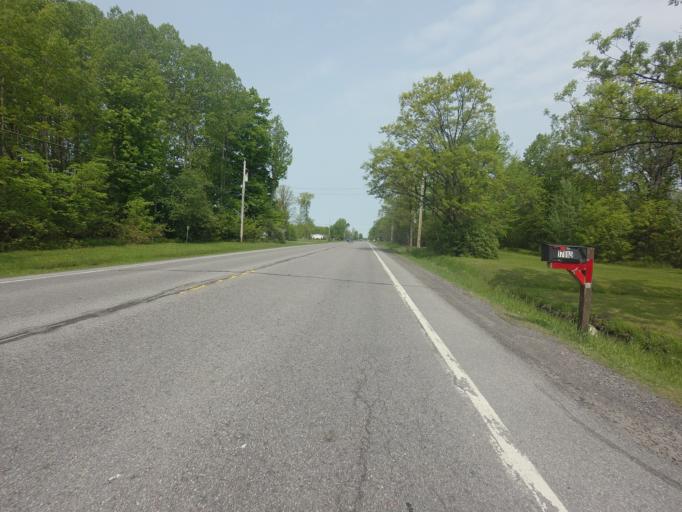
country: US
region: New York
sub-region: Jefferson County
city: Dexter
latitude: 44.0194
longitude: -76.0301
